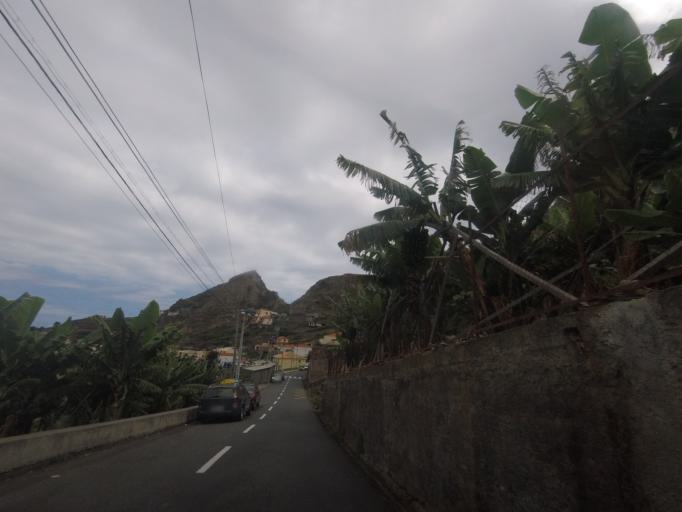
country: PT
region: Madeira
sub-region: Ribeira Brava
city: Campanario
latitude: 32.6586
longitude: -16.9975
